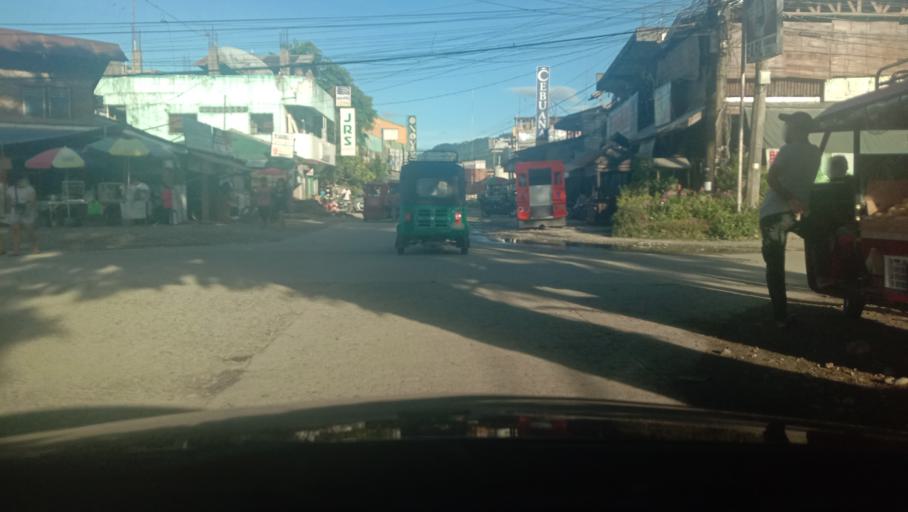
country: PH
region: Caraga
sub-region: Province of Agusan del Sur
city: Alegria
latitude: 8.5091
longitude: 125.9759
